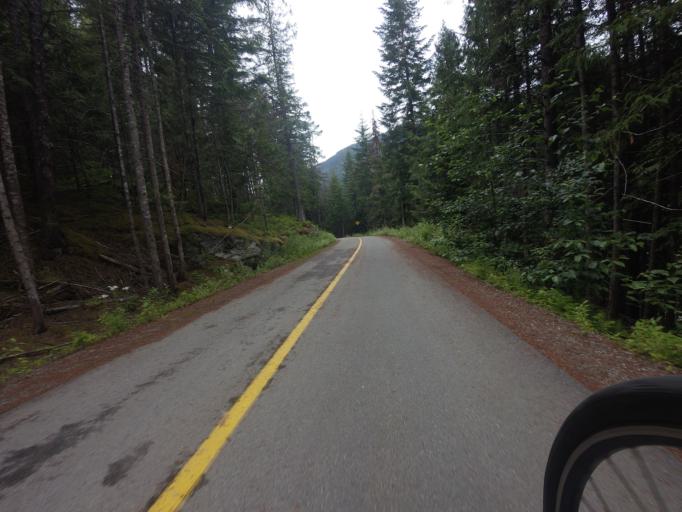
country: CA
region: British Columbia
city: Whistler
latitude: 50.0865
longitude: -123.0312
